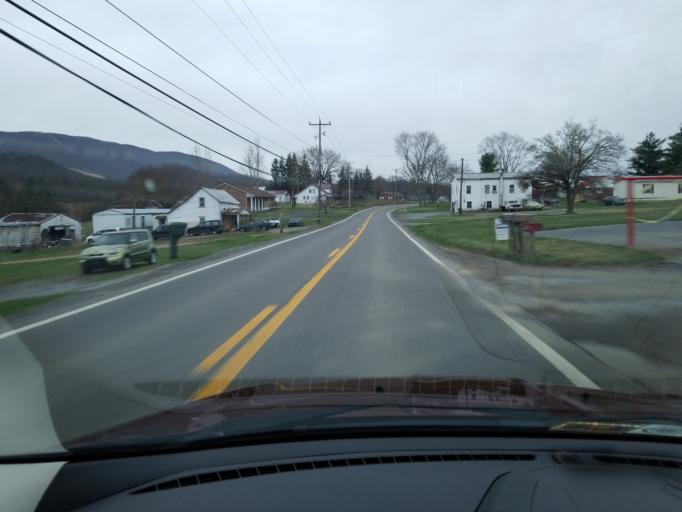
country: US
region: Virginia
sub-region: Giles County
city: Pearisburg
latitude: 37.4027
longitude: -80.7626
